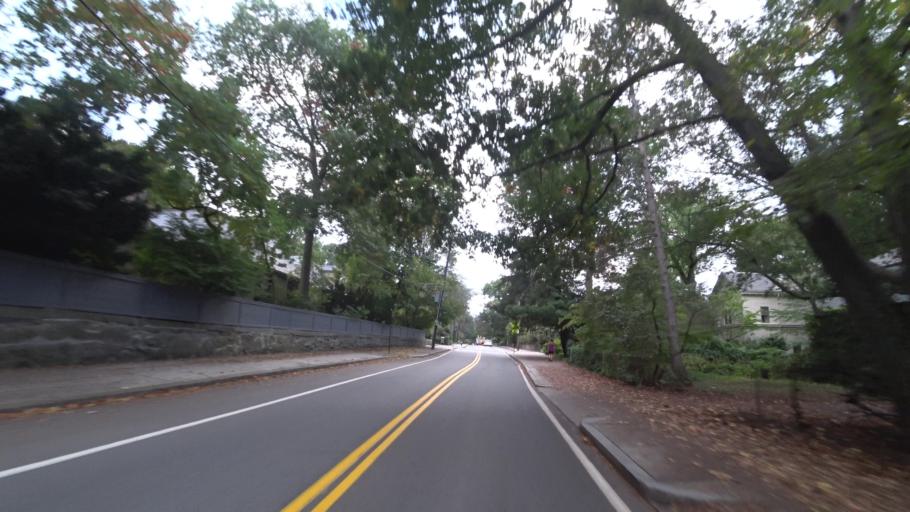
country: US
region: Massachusetts
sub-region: Norfolk County
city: Brookline
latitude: 42.3300
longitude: -71.1218
